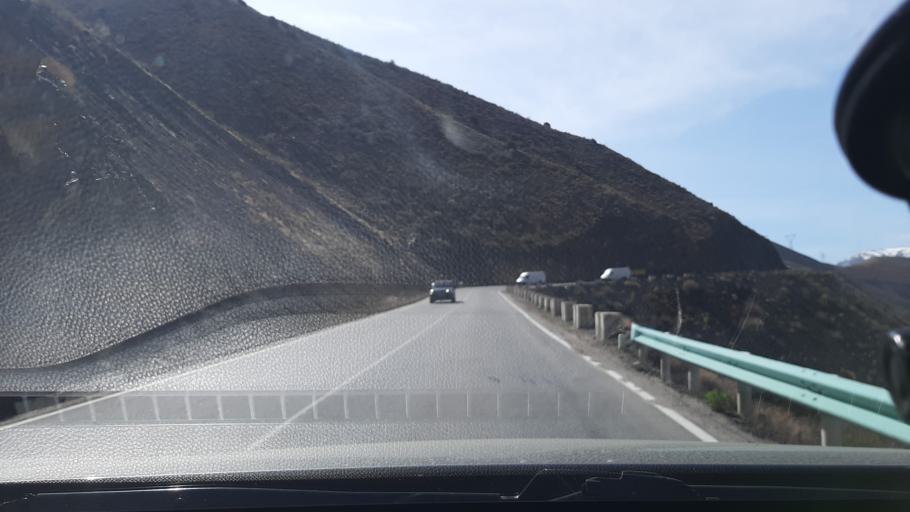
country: TJ
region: Viloyati Sughd
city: Ayni
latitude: 39.4483
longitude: 68.5468
